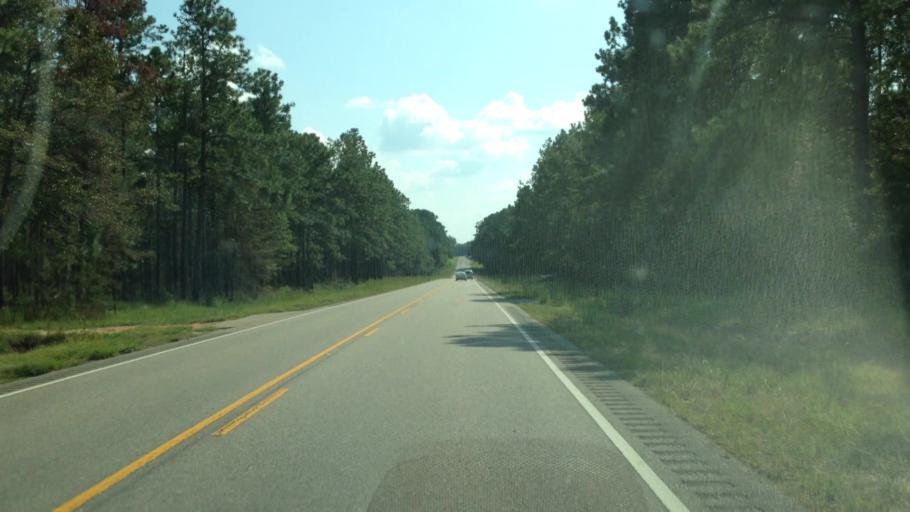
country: US
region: Florida
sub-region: Okaloosa County
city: Crestview
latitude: 31.0000
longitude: -86.6261
